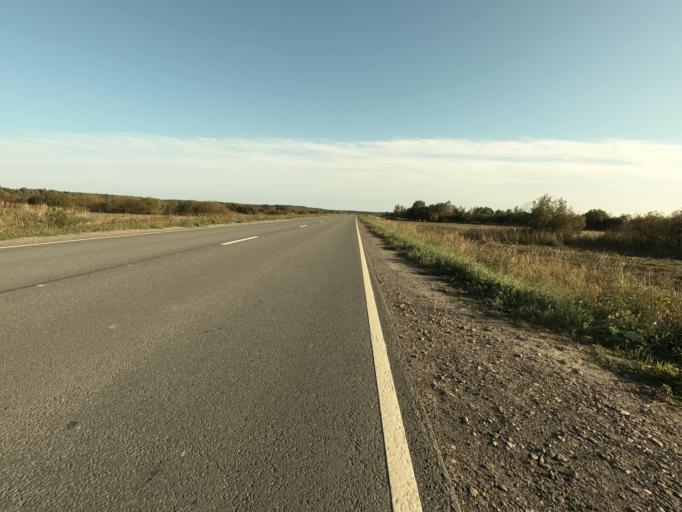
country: RU
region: St.-Petersburg
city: Sapernyy
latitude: 59.7455
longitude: 30.6451
